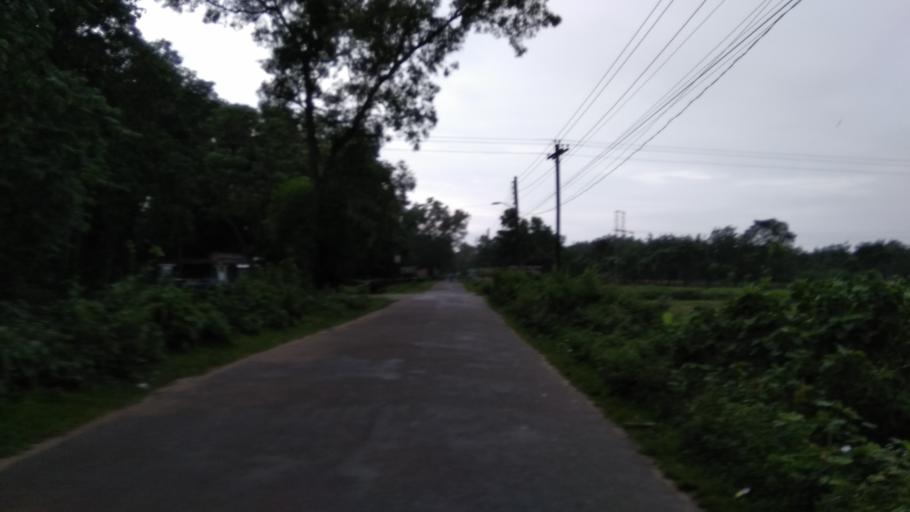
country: IN
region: Tripura
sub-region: Dhalai
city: Kamalpur
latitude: 24.3023
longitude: 91.7344
